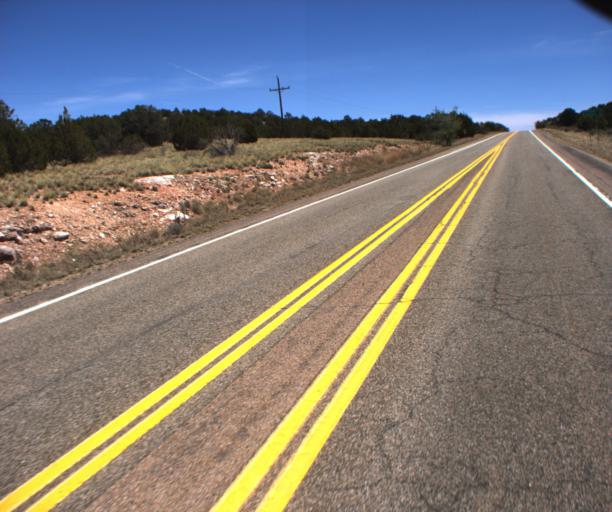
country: US
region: Arizona
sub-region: Mohave County
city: Peach Springs
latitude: 35.5280
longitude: -113.2236
